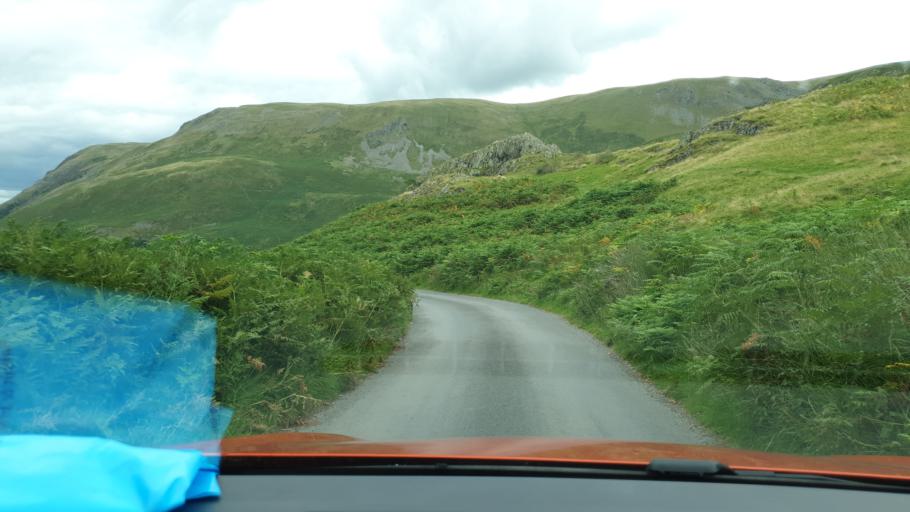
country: GB
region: England
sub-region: Cumbria
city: Penrith
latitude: 54.5653
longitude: -2.8733
